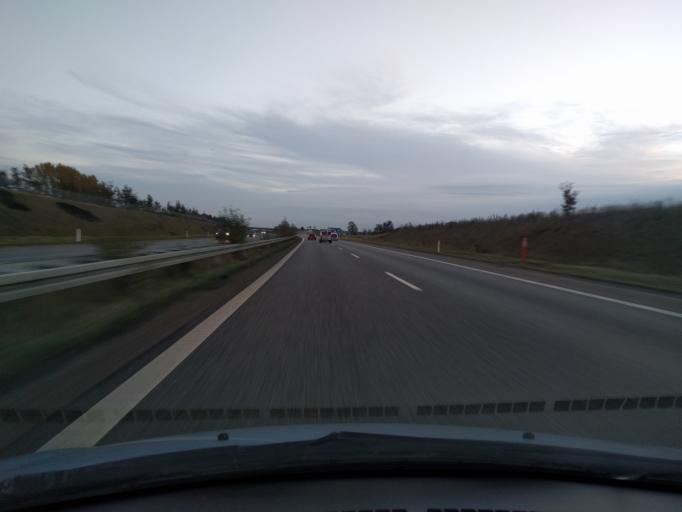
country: DK
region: South Denmark
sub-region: Faaborg-Midtfyn Kommune
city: Arslev
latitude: 55.3122
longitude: 10.4373
